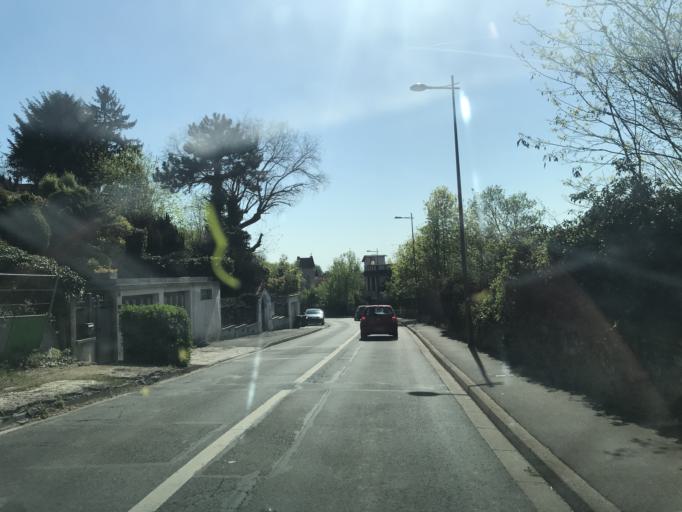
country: FR
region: Ile-de-France
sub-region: Departement du Val-de-Marne
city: Chennevieres-sur-Marne
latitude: 48.7921
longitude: 2.5256
